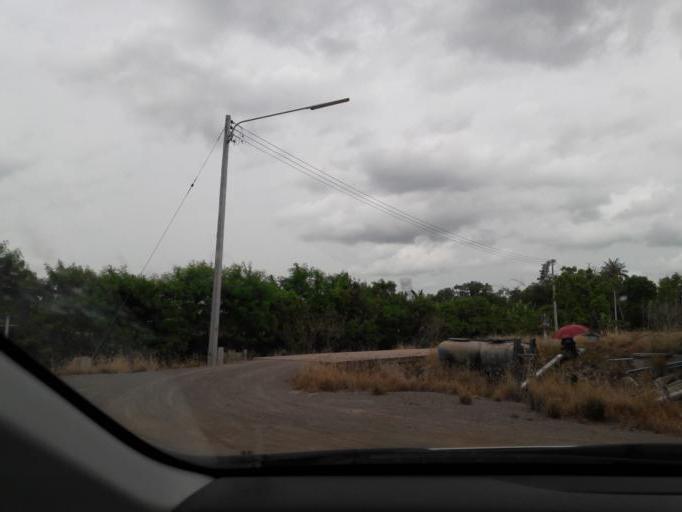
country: TH
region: Samut Sakhon
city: Ban Phaeo
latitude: 13.6017
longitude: 100.0258
